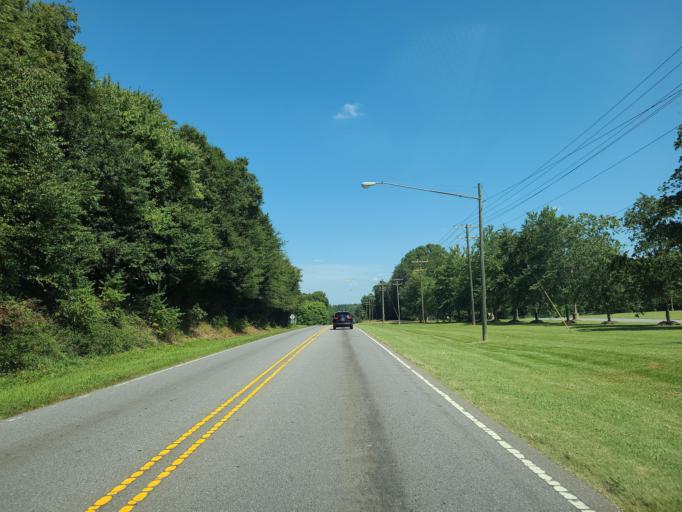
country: US
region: North Carolina
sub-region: Lincoln County
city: Lincolnton
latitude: 35.4563
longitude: -81.2426
